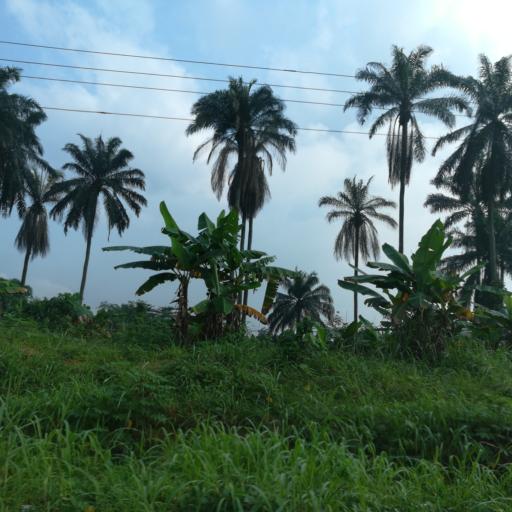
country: NG
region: Rivers
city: Okrika
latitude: 4.7743
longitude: 7.1596
